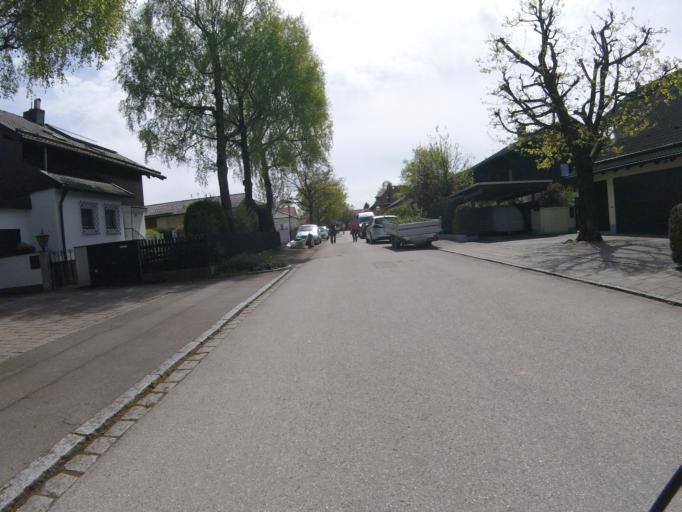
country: DE
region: Bavaria
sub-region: Upper Bavaria
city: Hohenbrunn
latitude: 48.0503
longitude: 11.6973
